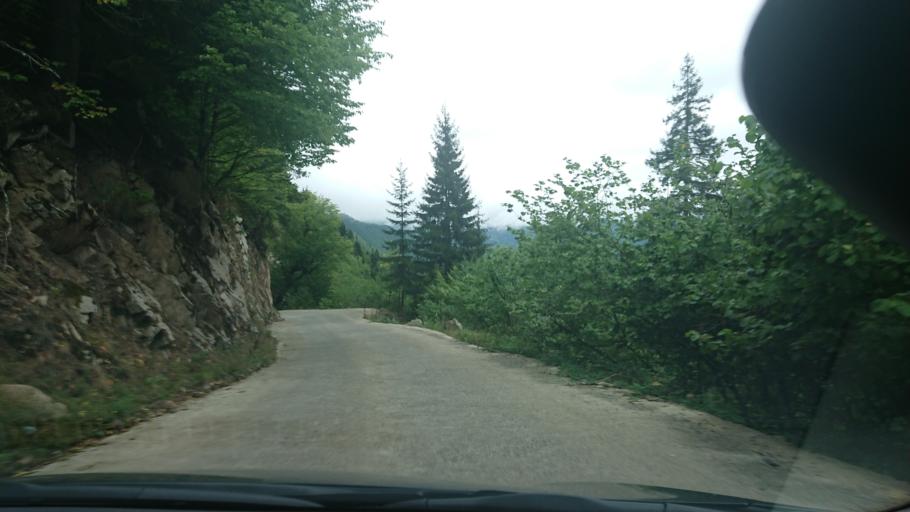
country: TR
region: Gumushane
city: Kurtun
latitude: 40.6804
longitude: 39.0496
